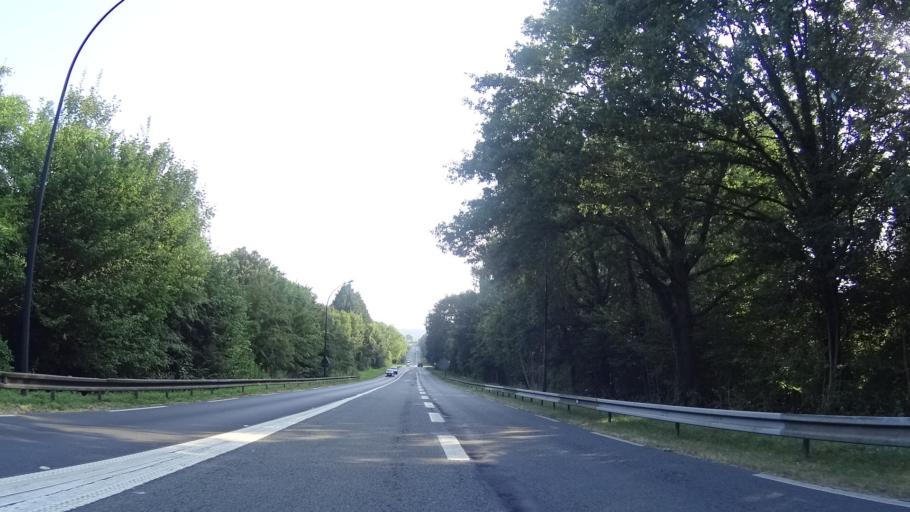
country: FR
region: Ile-de-France
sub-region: Departement du Val-d'Oise
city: Luzarches
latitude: 49.1031
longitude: 2.4235
